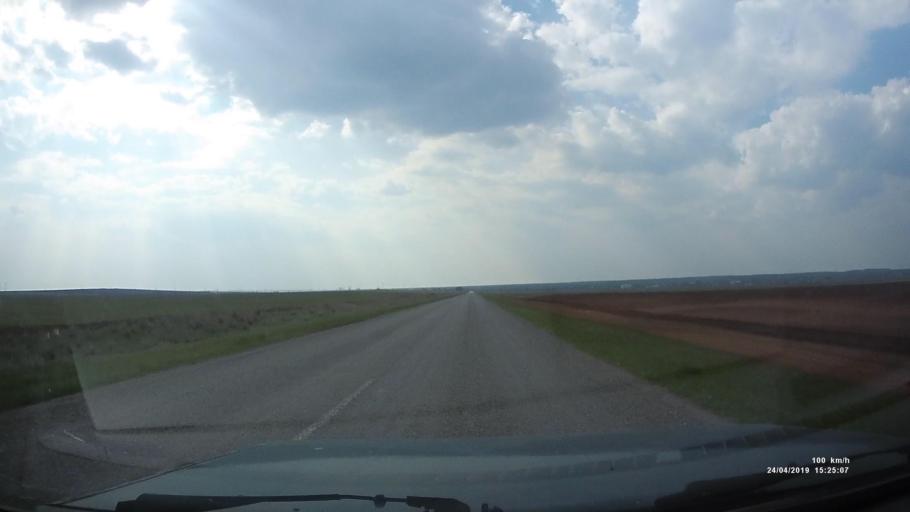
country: RU
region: Rostov
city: Remontnoye
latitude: 46.5509
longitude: 43.0543
